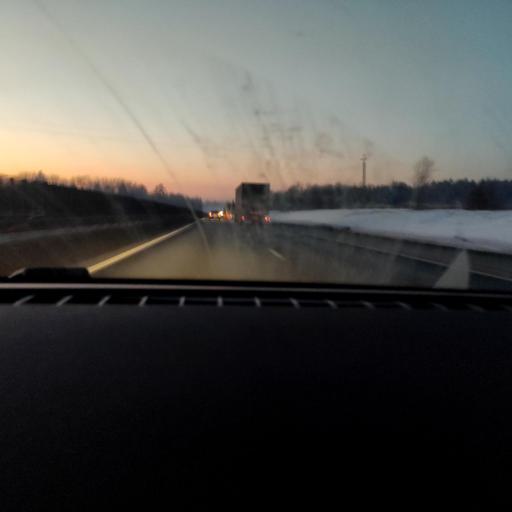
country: RU
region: Samara
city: Bereza
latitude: 53.4744
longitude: 50.1602
